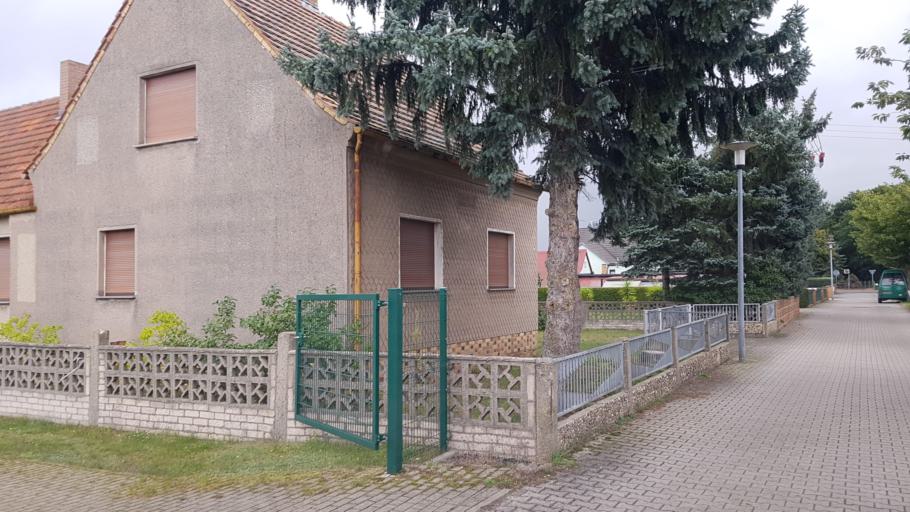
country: DE
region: Brandenburg
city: Tettau
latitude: 51.4240
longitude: 13.7262
